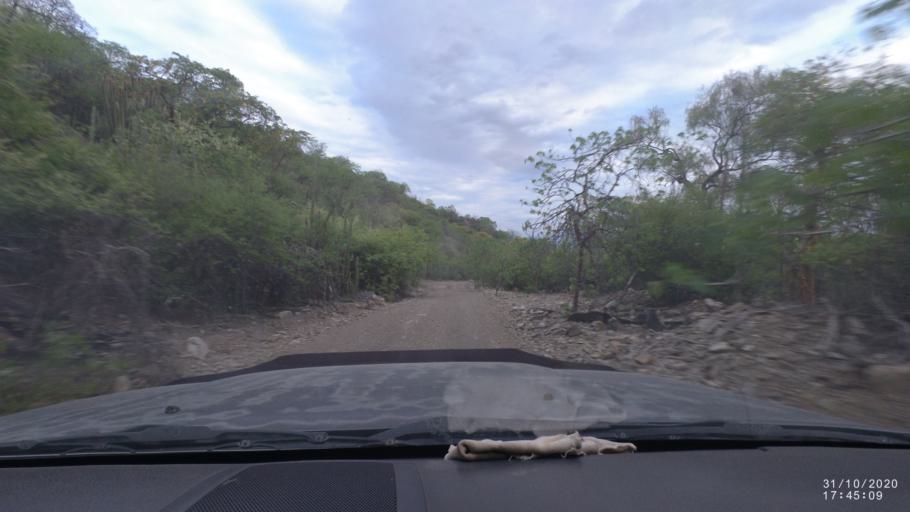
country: BO
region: Chuquisaca
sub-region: Provincia Zudanez
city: Mojocoya
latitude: -18.6138
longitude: -64.5439
